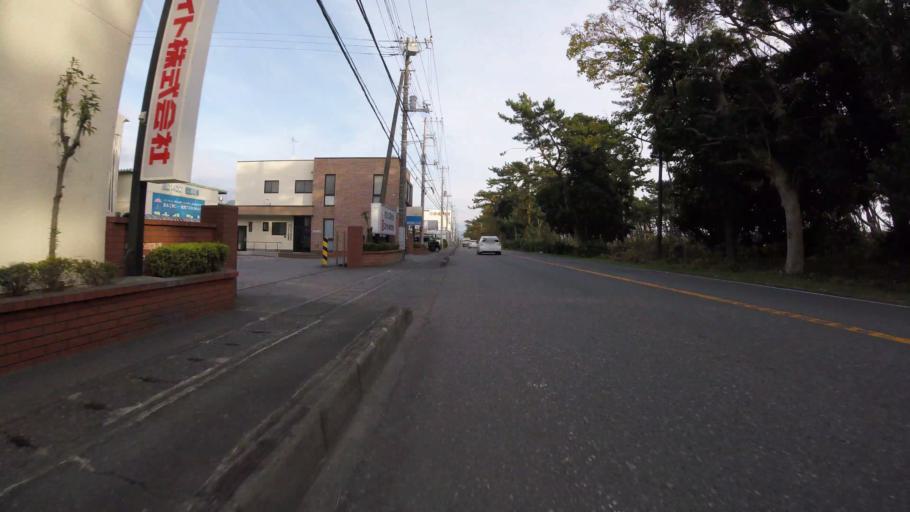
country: JP
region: Shizuoka
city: Fuji
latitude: 35.1314
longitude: 138.7638
